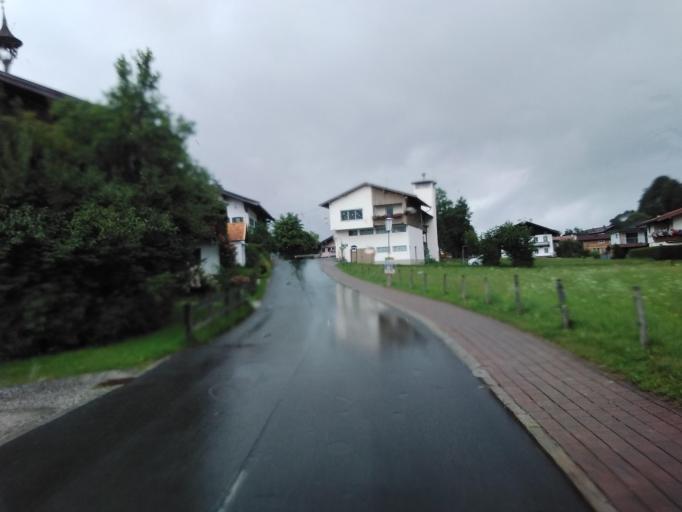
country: AT
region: Tyrol
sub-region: Politischer Bezirk Kitzbuhel
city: Schwendt
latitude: 47.6332
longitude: 12.3911
